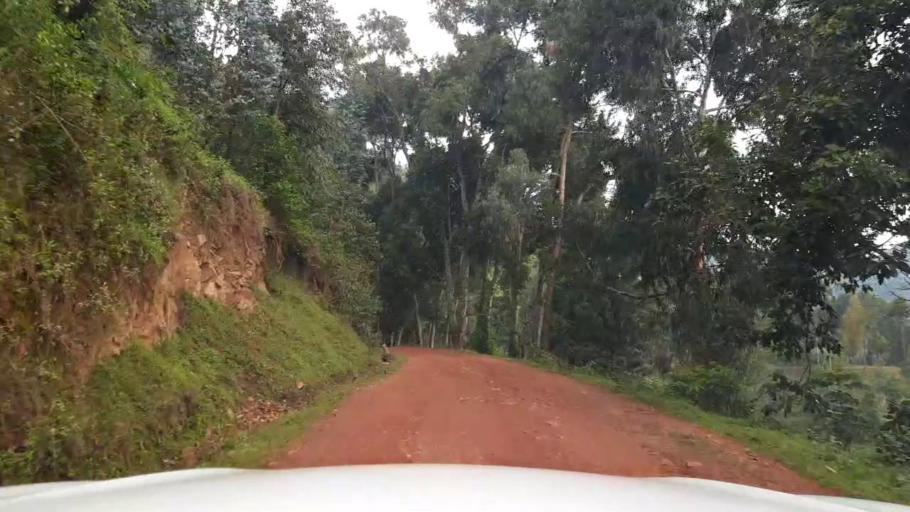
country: UG
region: Western Region
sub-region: Kisoro District
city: Kisoro
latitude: -1.3974
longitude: 29.8028
